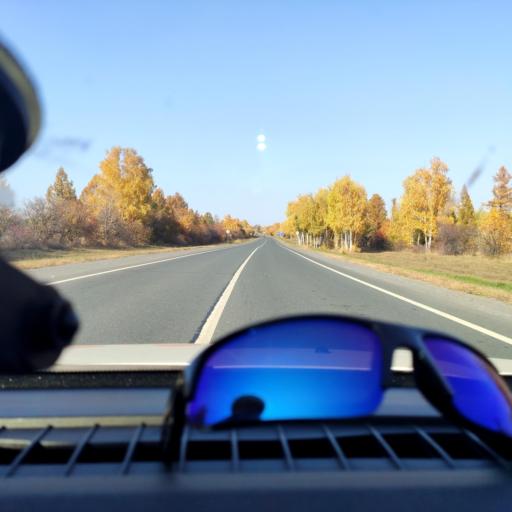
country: RU
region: Samara
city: Bereza
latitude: 53.4779
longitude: 50.1166
